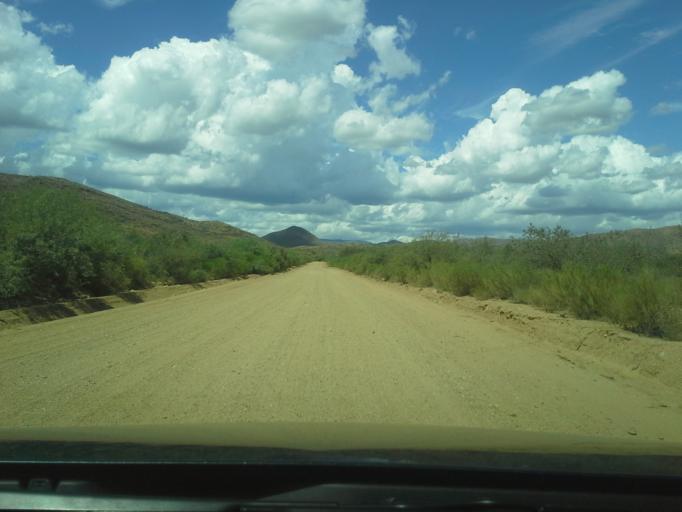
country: US
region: Arizona
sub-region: Yavapai County
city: Cordes Lakes
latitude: 34.2566
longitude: -112.1764
